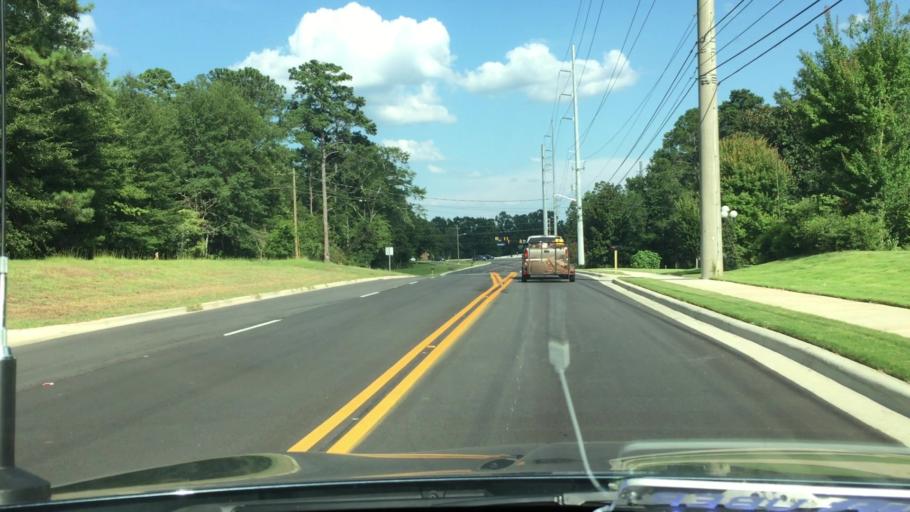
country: US
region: Alabama
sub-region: Lee County
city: Auburn
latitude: 32.5905
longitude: -85.4623
